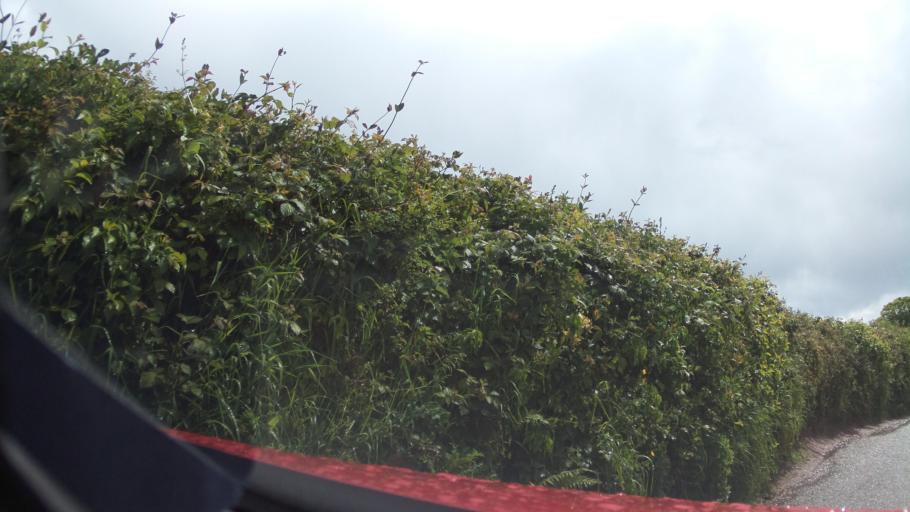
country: GB
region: England
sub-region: Devon
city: Dartmouth
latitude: 50.3523
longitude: -3.5378
